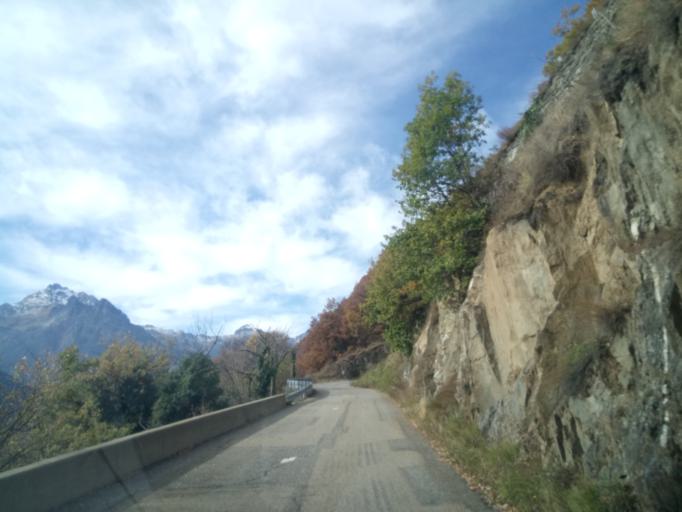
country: FR
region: Rhone-Alpes
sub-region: Departement de la Savoie
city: La Chambre
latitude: 45.3725
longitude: 6.3039
